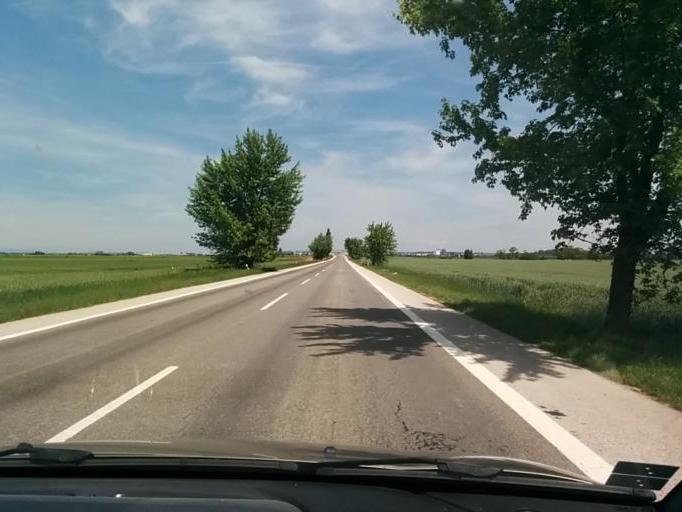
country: SK
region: Trnavsky
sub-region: Okres Galanta
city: Galanta
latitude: 48.2511
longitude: 17.7075
